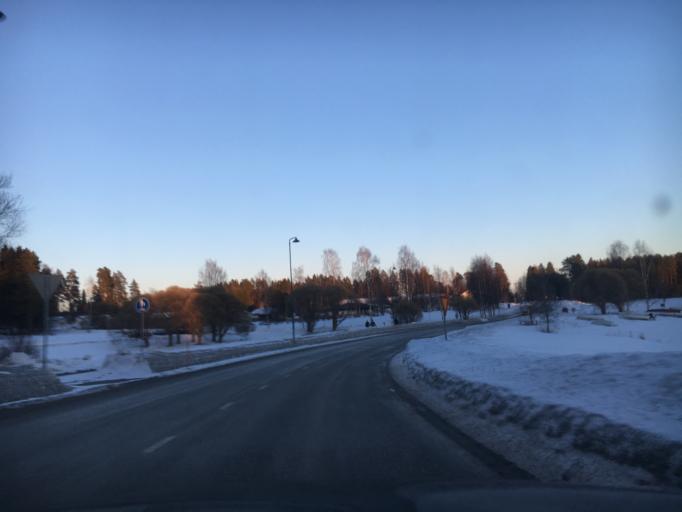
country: FI
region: Kainuu
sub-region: Kajaani
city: Kajaani
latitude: 64.2296
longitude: 27.7701
